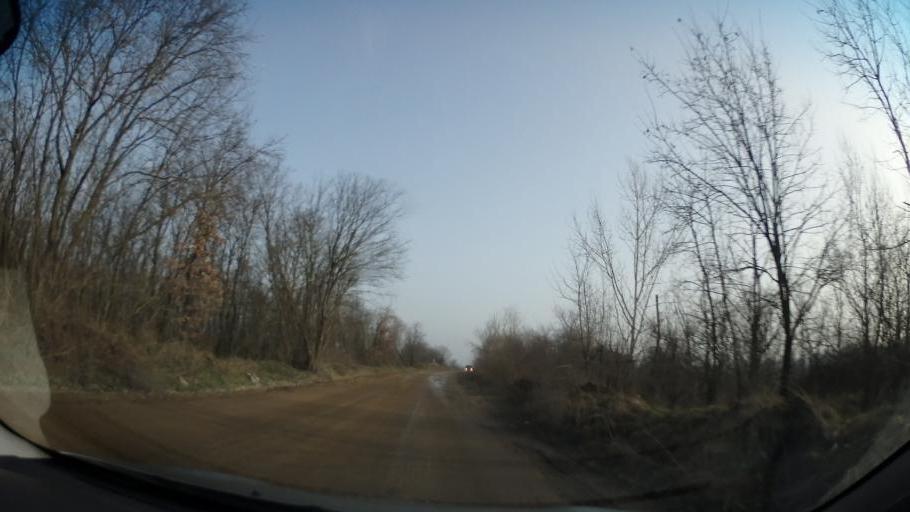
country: CZ
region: South Moravian
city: Hrusovany u Brna
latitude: 49.0276
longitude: 16.5594
